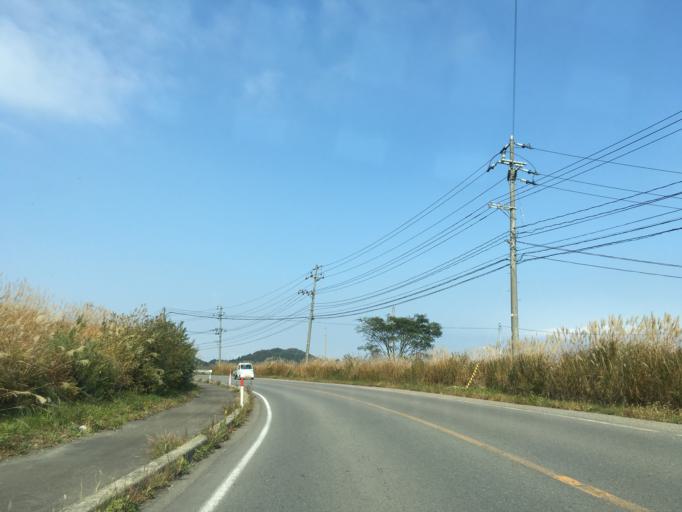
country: JP
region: Fukushima
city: Inawashiro
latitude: 37.4929
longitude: 140.0082
